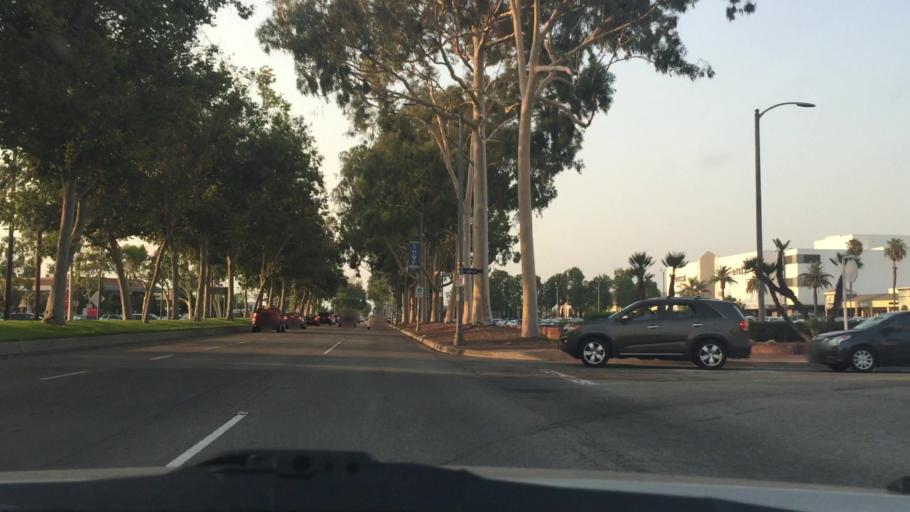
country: US
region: California
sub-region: Los Angeles County
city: Lakewood
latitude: 33.8479
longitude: -118.1424
